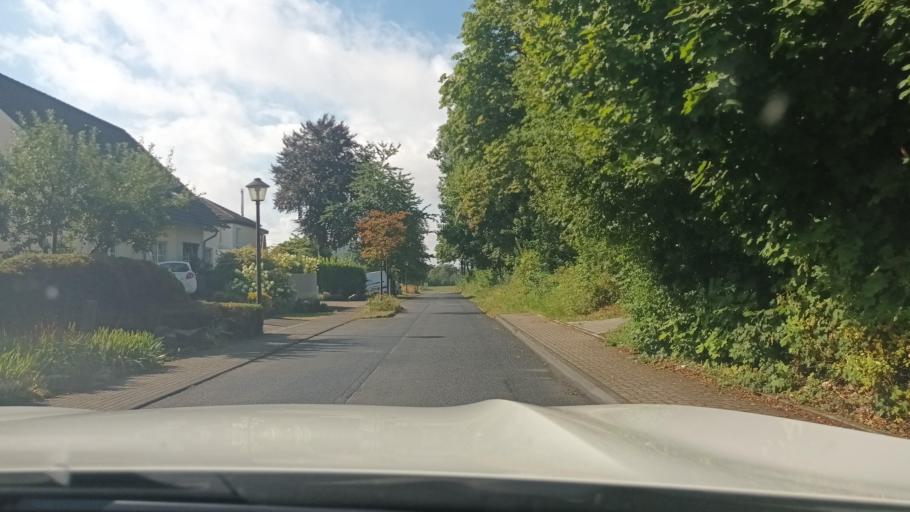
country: DE
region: North Rhine-Westphalia
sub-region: Regierungsbezirk Koln
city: Hennef
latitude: 50.7967
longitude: 7.3005
